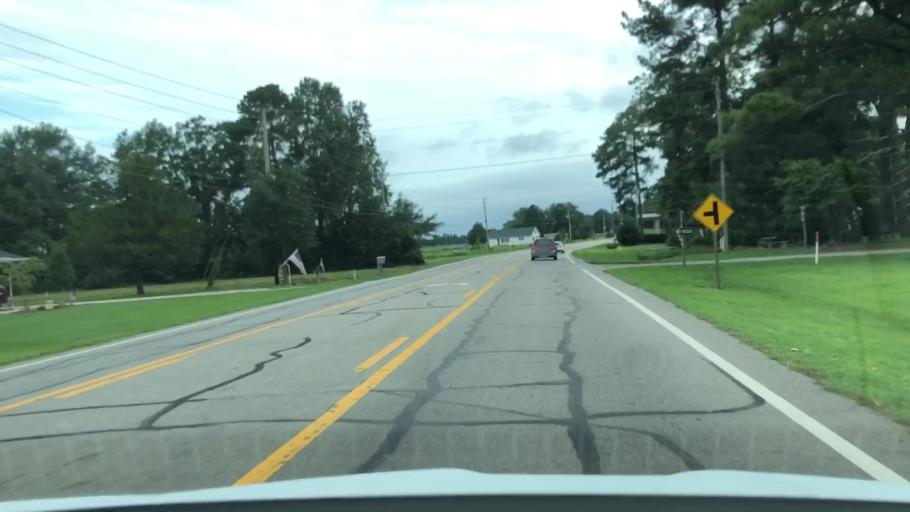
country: US
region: North Carolina
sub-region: Lenoir County
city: Kinston
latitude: 35.2075
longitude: -77.5658
